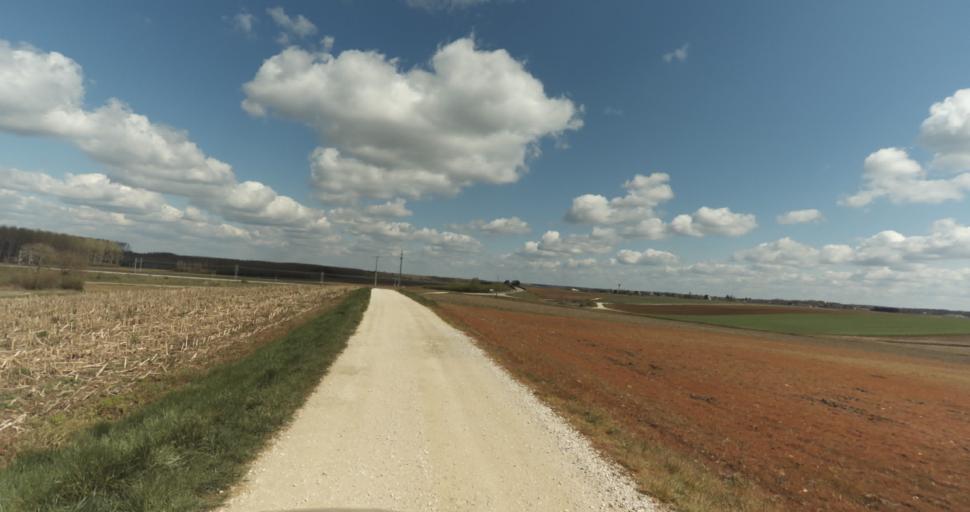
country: FR
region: Bourgogne
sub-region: Departement de la Cote-d'Or
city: Auxonne
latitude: 47.2206
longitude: 5.4227
